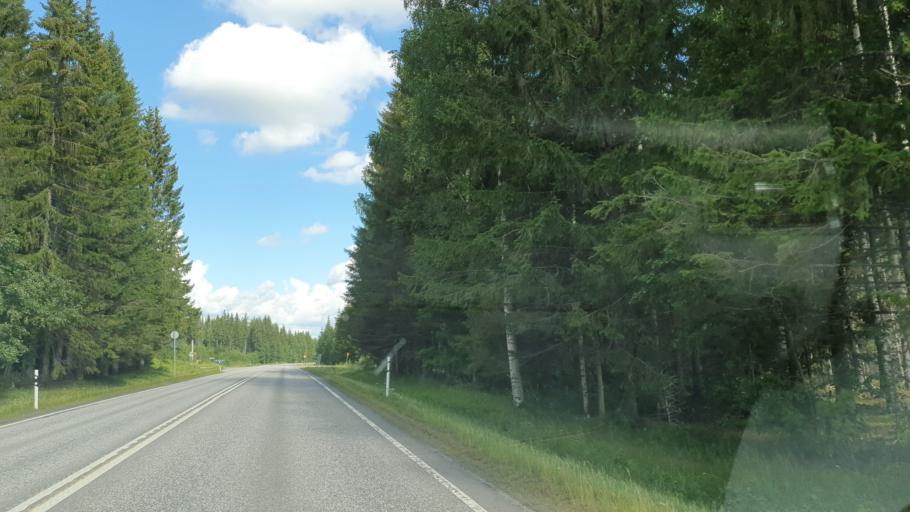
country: FI
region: Northern Savo
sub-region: Ylae-Savo
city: Sonkajaervi
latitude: 63.7455
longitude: 27.3833
